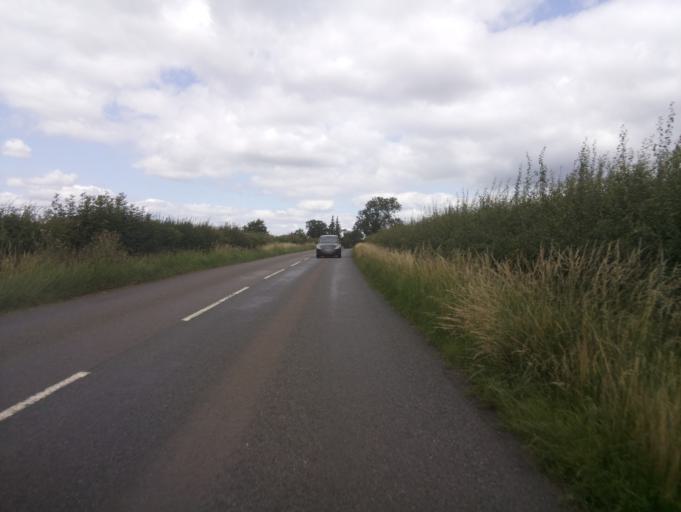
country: GB
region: England
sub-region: Buckinghamshire
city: Newton Longville
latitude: 51.9763
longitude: -0.8231
